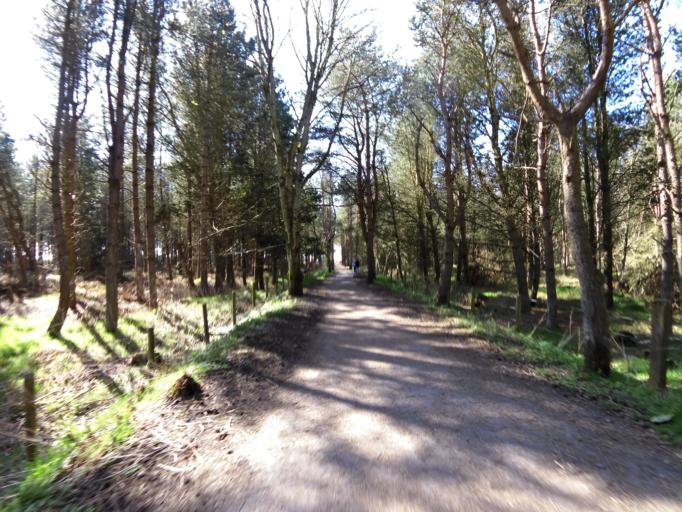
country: GB
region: Scotland
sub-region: Angus
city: Montrose
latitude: 56.7409
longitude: -2.4517
